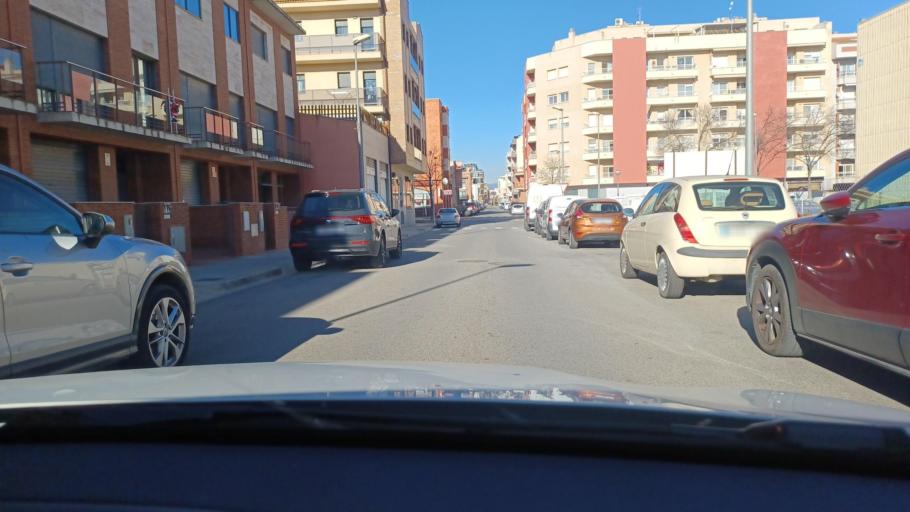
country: ES
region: Catalonia
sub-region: Provincia de Tarragona
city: Amposta
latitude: 40.7033
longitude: 0.5776
